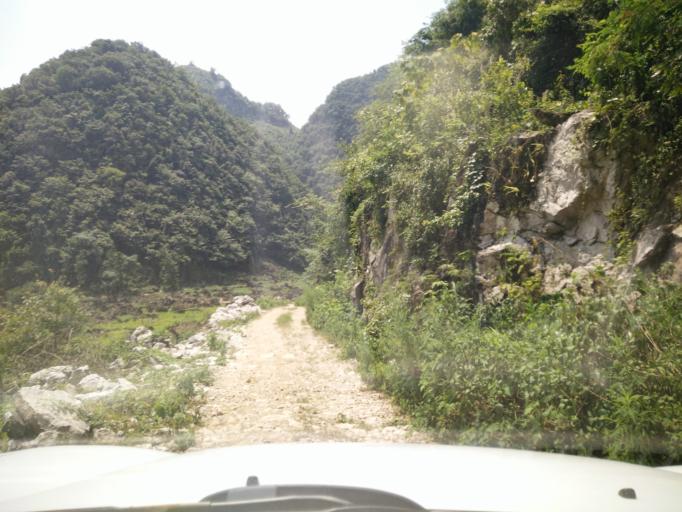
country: CN
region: Guangxi Zhuangzu Zizhiqu
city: Xinzhou
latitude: 25.0113
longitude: 105.7056
